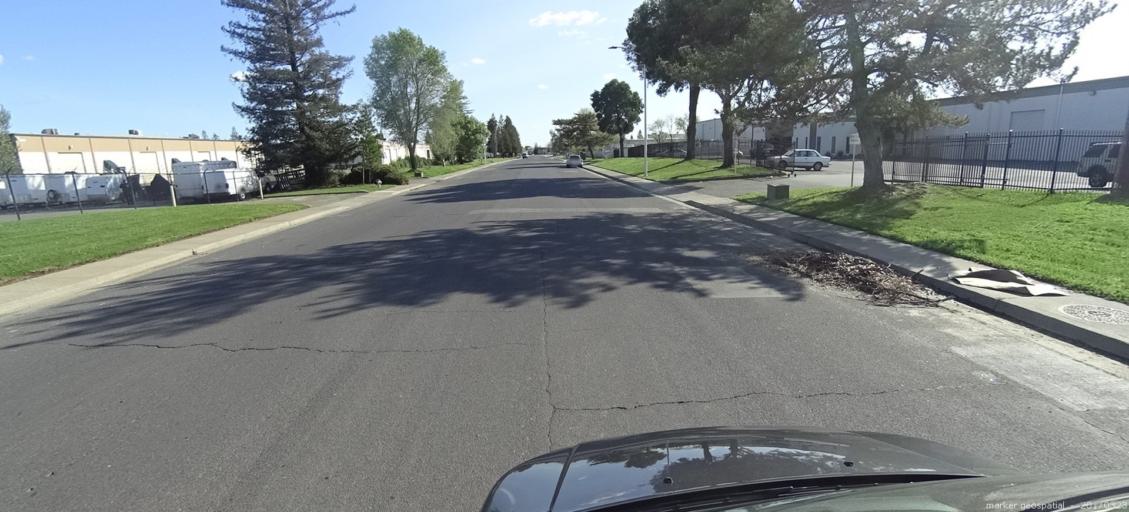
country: US
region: California
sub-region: Sacramento County
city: Rosemont
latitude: 38.5230
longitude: -121.3759
